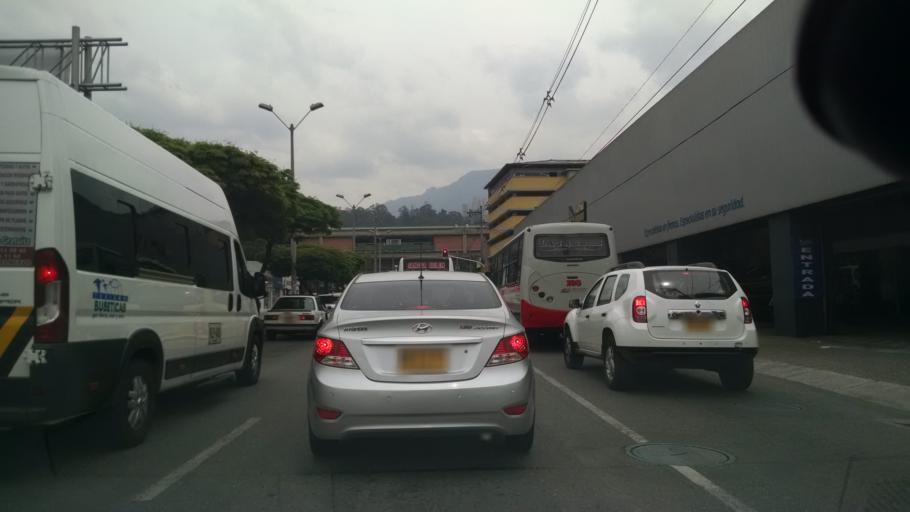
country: CO
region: Antioquia
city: Medellin
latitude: 6.2389
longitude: -75.5744
